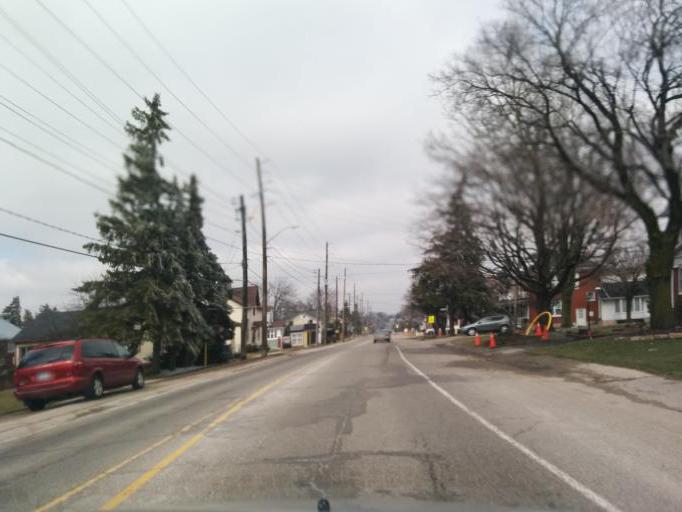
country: CA
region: Ontario
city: Waterloo
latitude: 43.5335
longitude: -80.5545
